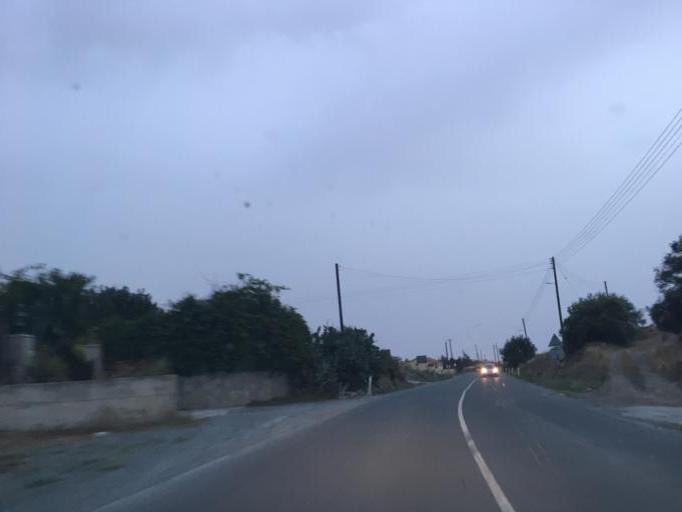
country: CY
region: Limassol
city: Parekklisha
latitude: 34.7518
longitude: 33.1625
